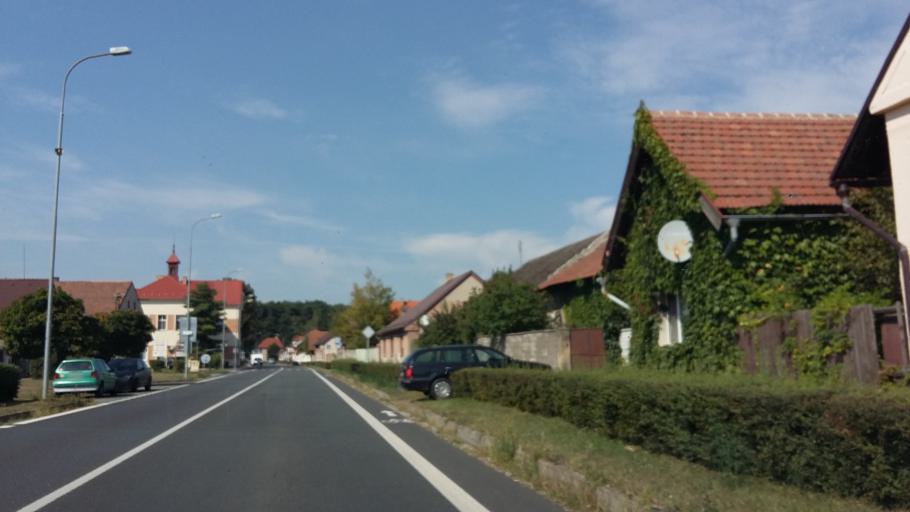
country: CZ
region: Central Bohemia
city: Velky Osek
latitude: 50.0980
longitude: 15.1861
